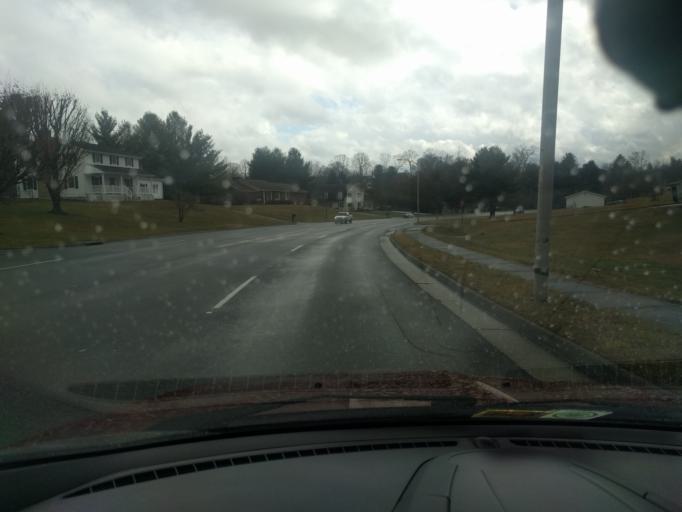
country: US
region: Virginia
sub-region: Pulaski County
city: Pulaski
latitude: 37.0602
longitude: -80.7572
